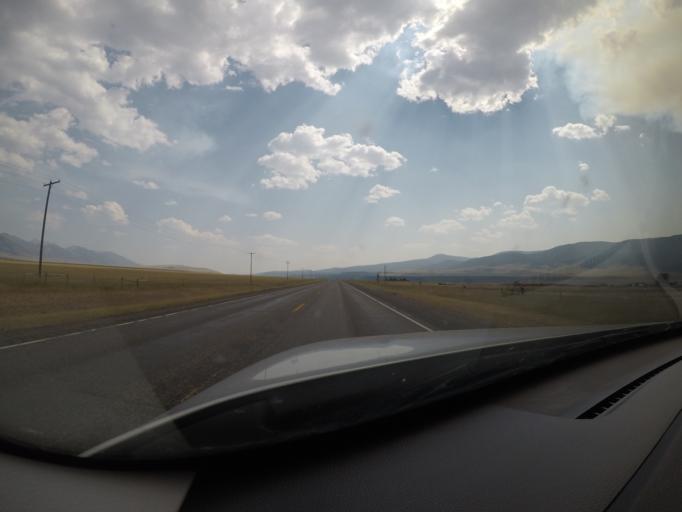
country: US
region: Montana
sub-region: Gallatin County
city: Big Sky
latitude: 45.0114
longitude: -111.6483
